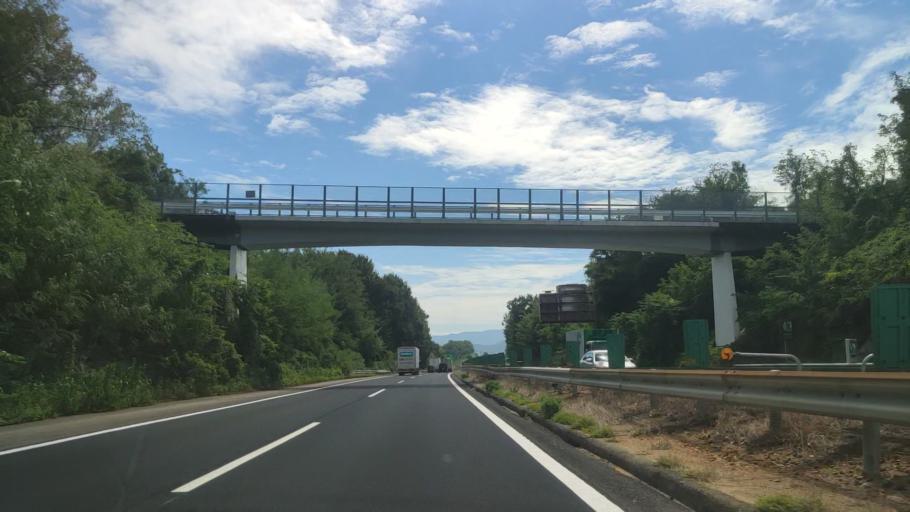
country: JP
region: Aichi
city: Okazaki
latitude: 34.9540
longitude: 137.1958
